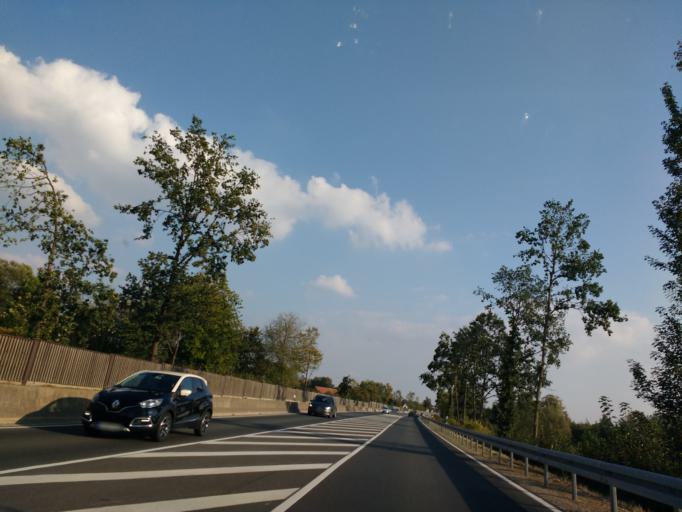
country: DE
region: North Rhine-Westphalia
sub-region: Regierungsbezirk Detmold
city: Steinheim
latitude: 51.8752
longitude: 9.1021
